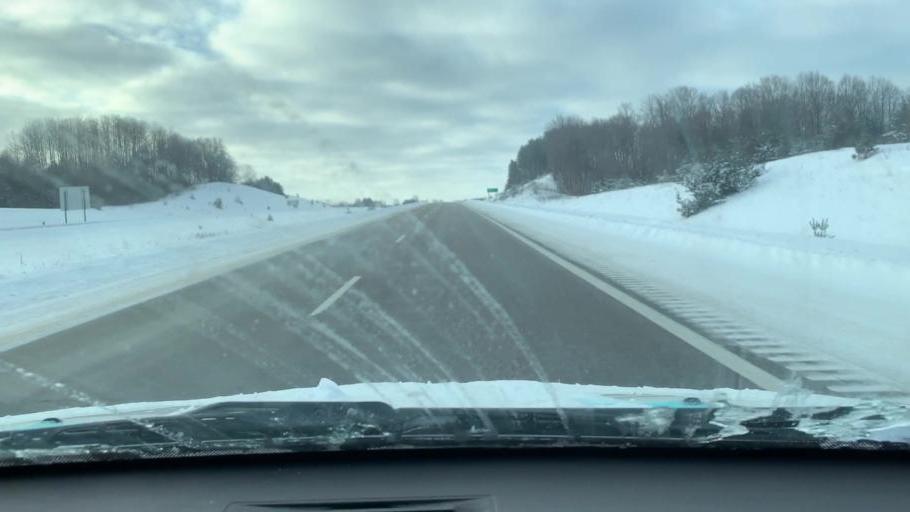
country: US
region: Michigan
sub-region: Wexford County
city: Manton
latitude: 44.3944
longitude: -85.3825
